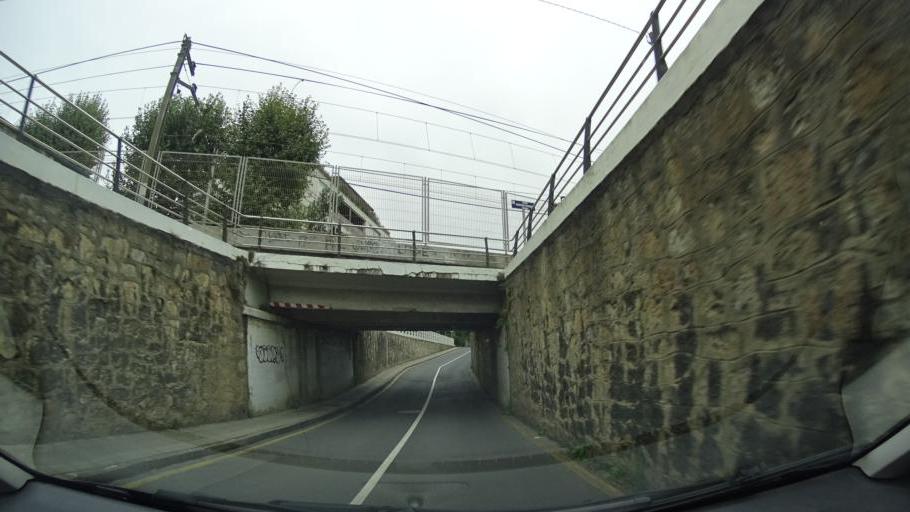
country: ES
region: Basque Country
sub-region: Bizkaia
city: Algorta
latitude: 43.3389
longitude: -3.0080
